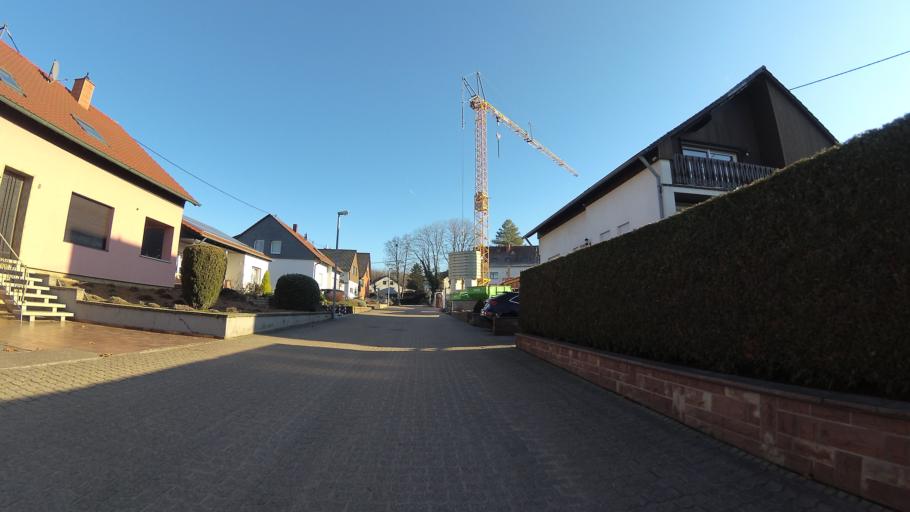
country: DE
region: Saarland
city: Wallerfangen
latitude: 49.3128
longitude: 6.7165
